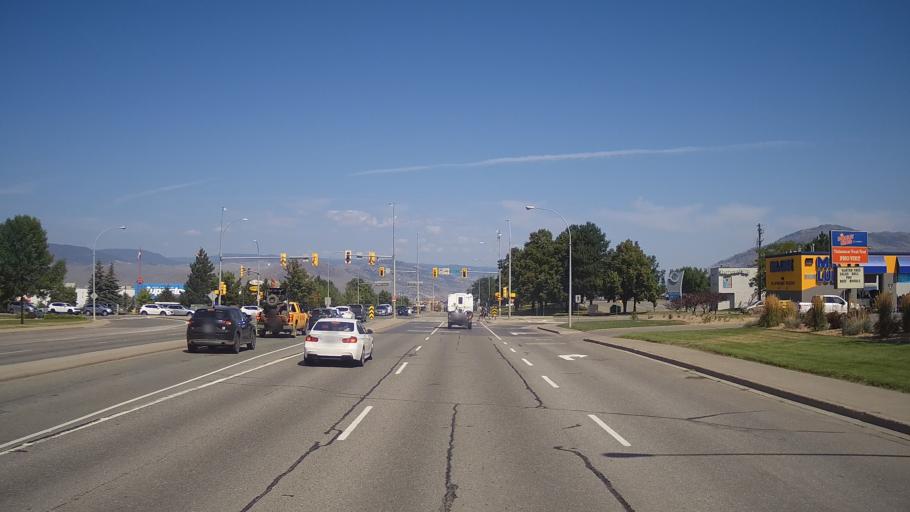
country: CA
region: British Columbia
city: Kamloops
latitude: 50.6662
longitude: -120.3540
